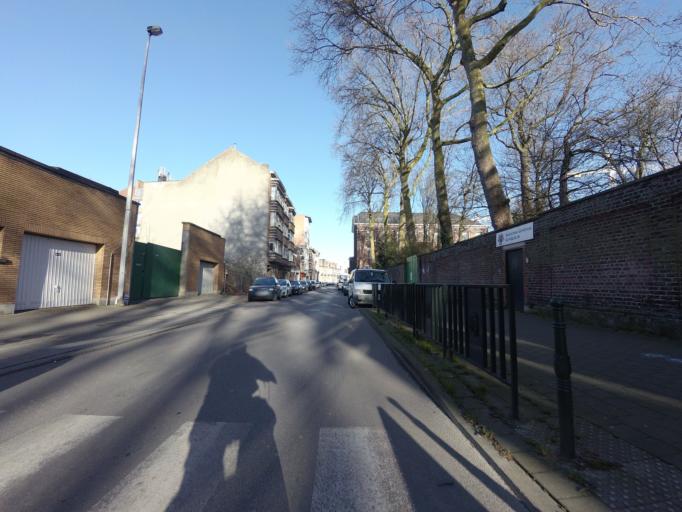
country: BE
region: Brussels Capital
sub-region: Bruxelles-Capitale
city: Brussels
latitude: 50.8724
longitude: 4.3493
